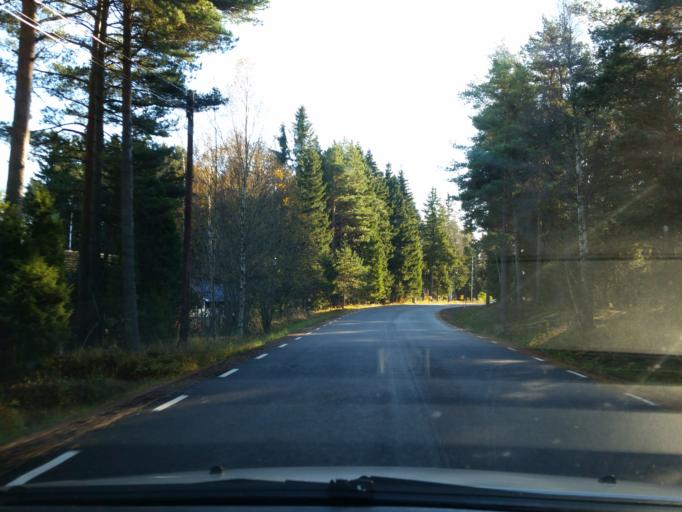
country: AX
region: Alands landsbygd
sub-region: Jomala
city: Jomala
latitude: 60.1997
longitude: 19.9577
